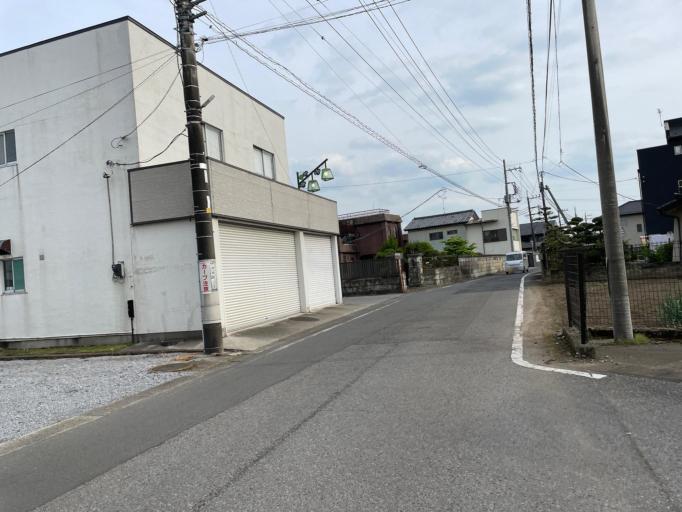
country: JP
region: Tochigi
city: Mibu
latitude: 36.4254
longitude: 139.8059
